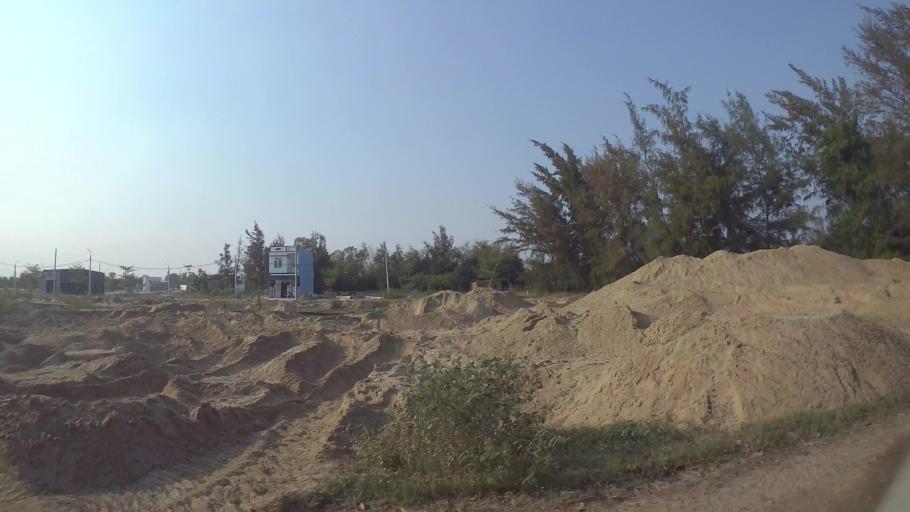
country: VN
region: Da Nang
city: Ngu Hanh Son
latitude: 15.9633
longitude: 108.2638
